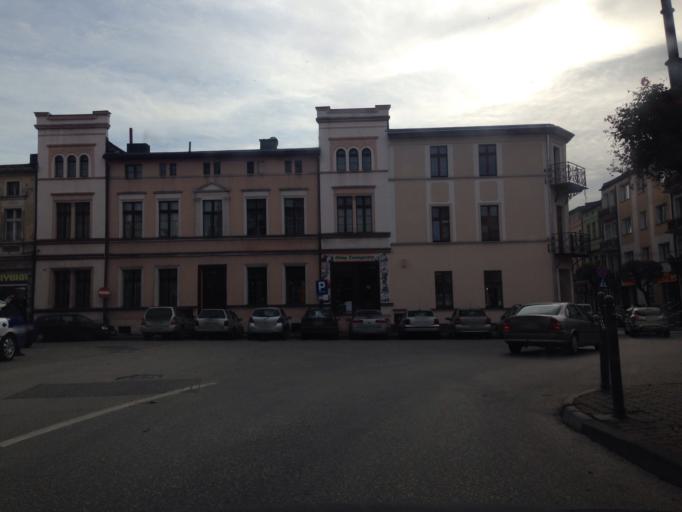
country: PL
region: Kujawsko-Pomorskie
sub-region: Powiat brodnicki
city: Brodnica
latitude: 53.2575
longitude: 19.4025
